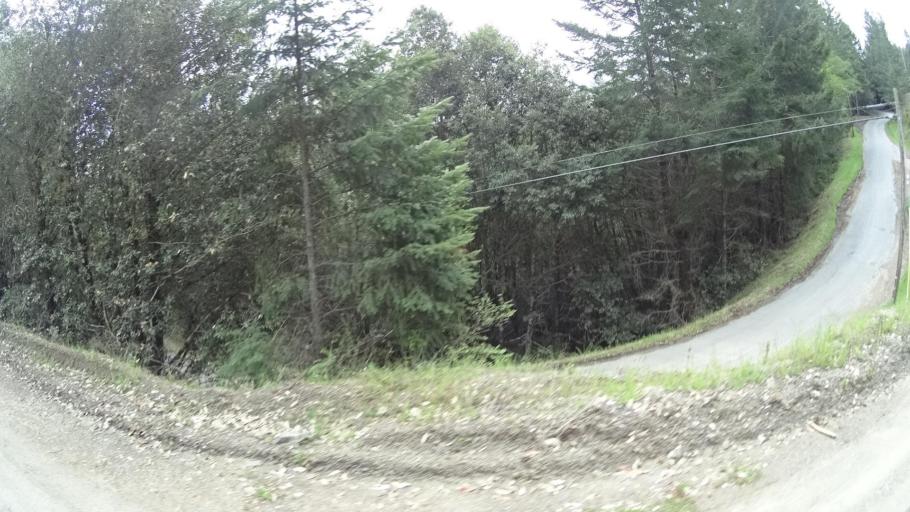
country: US
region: California
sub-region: Humboldt County
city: Blue Lake
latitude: 40.7625
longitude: -123.9578
